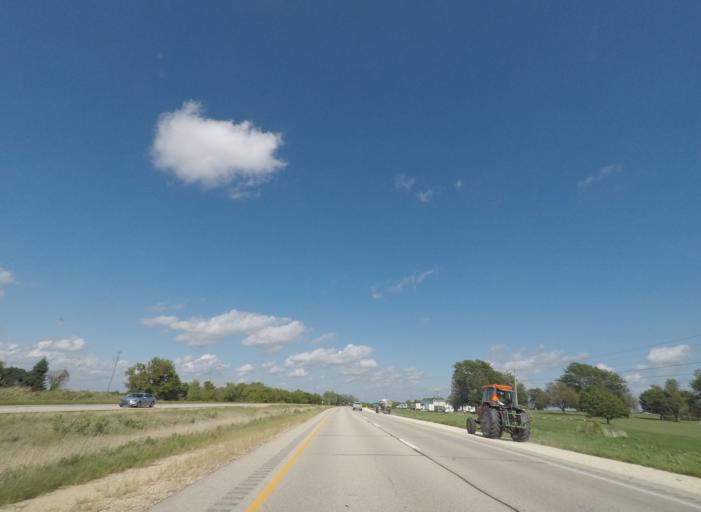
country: US
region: Iowa
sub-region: Dubuque County
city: Asbury
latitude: 42.4144
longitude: -90.7296
